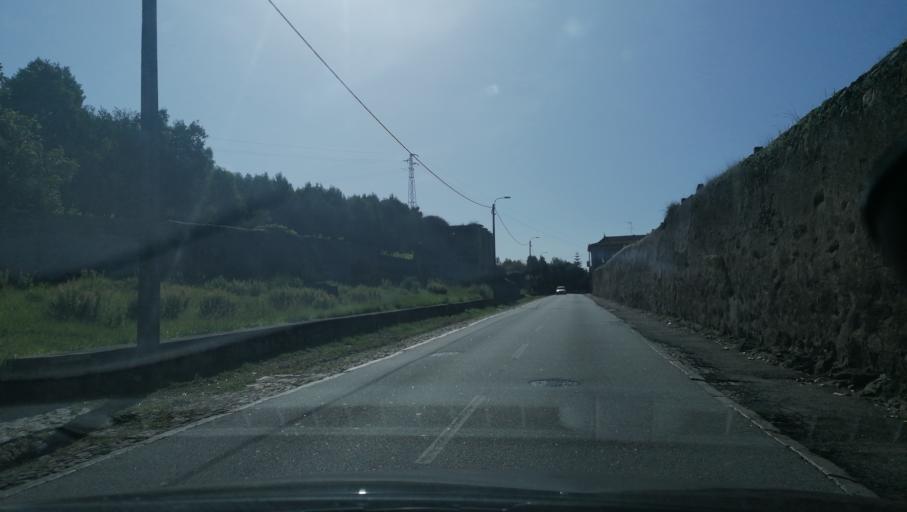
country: PT
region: Porto
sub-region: Vila Nova de Gaia
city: Arcozelo
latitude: 41.0577
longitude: -8.6268
